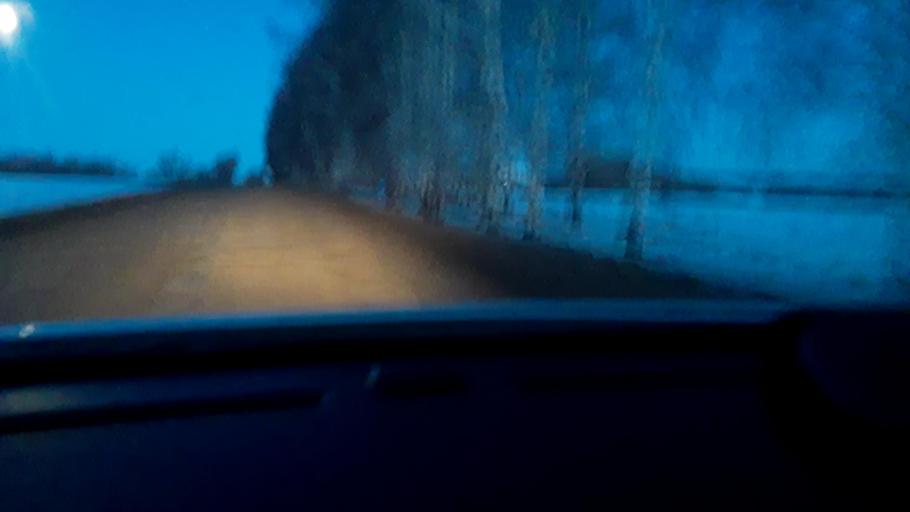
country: RU
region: Bashkortostan
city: Avdon
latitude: 54.3878
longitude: 55.7501
